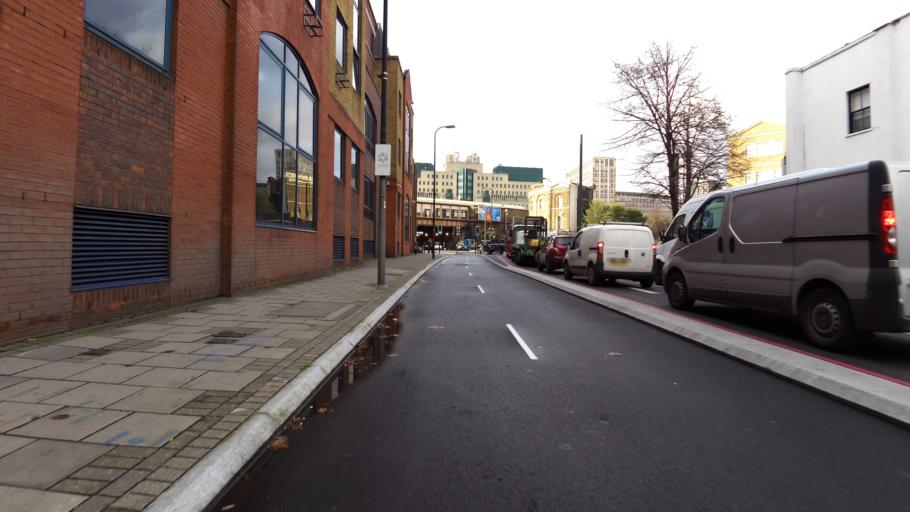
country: GB
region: England
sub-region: Greater London
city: Lambeth
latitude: 51.4857
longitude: -0.1210
